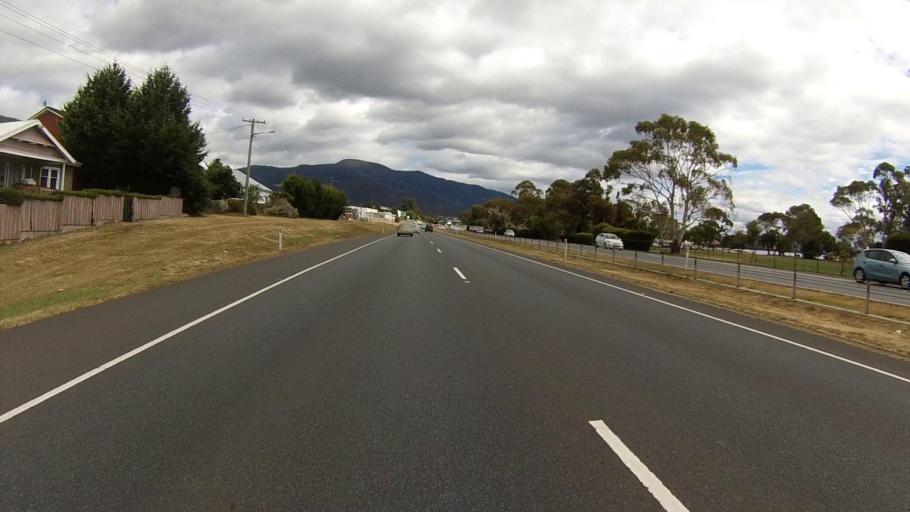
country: AU
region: Tasmania
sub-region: Glenorchy
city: Glenorchy
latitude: -42.8241
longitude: 147.2711
